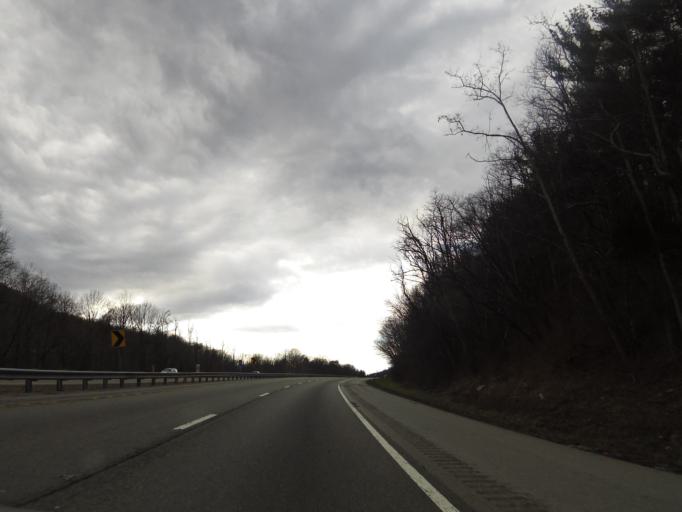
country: US
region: Tennessee
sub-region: Cumberland County
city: Fairfield Glade
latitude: 35.8986
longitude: -84.8502
